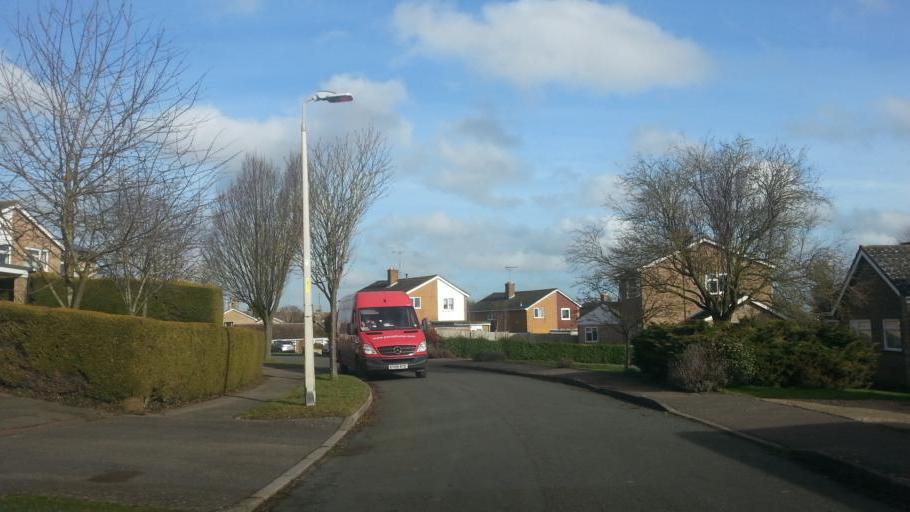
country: GB
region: England
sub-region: District of Rutland
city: Ketton
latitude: 52.6262
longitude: -0.5606
